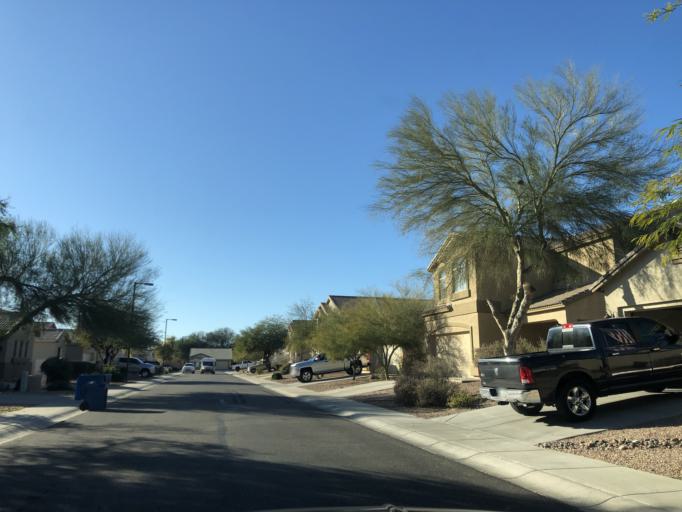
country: US
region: Arizona
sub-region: Maricopa County
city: Buckeye
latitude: 33.4380
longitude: -112.5695
